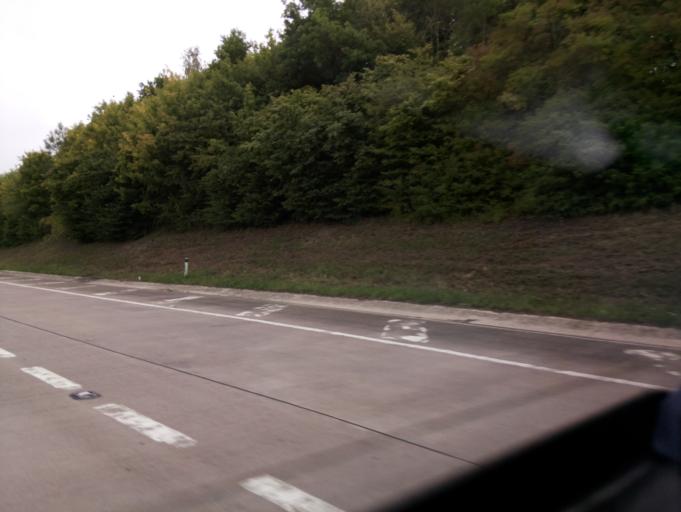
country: GB
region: England
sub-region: Gloucestershire
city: Cirencester
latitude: 51.7215
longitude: -1.9448
